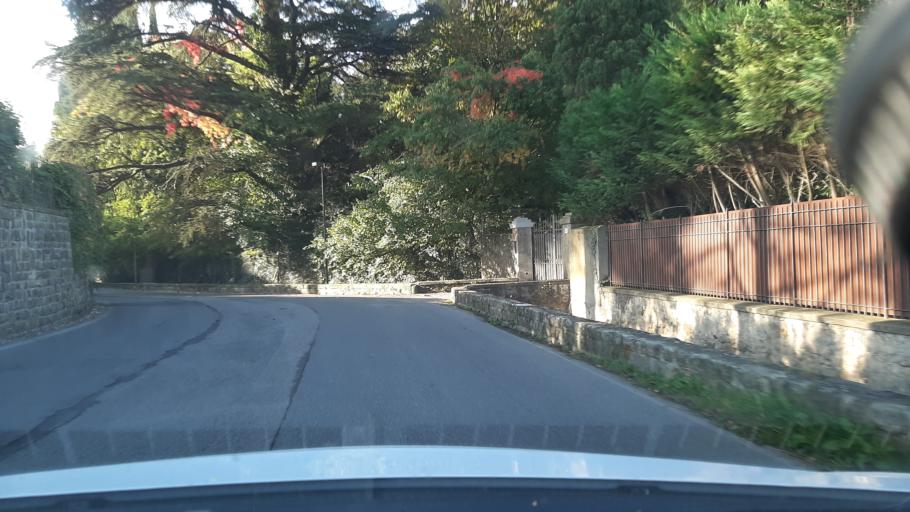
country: IT
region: Tuscany
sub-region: Province of Florence
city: Fiesole
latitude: 43.7885
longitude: 11.2940
